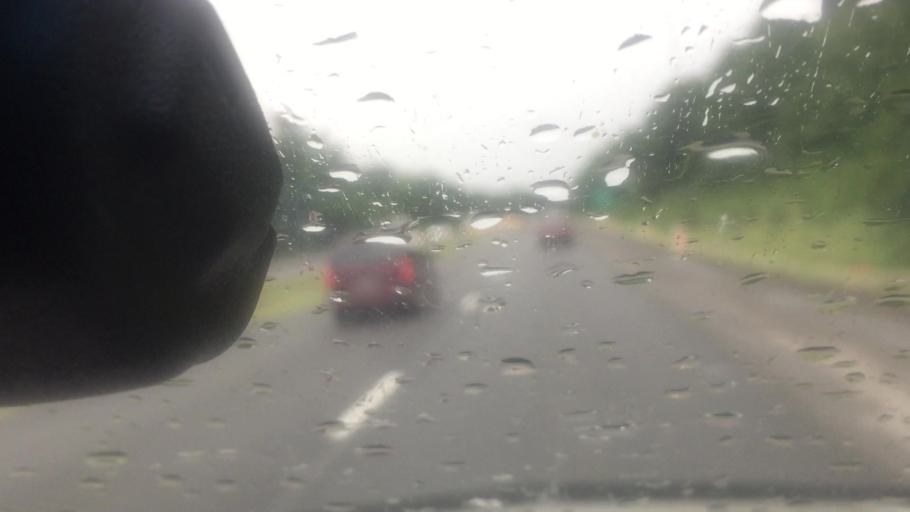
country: US
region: Illinois
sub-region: Sangamon County
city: Southern View
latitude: 39.7494
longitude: -89.6175
